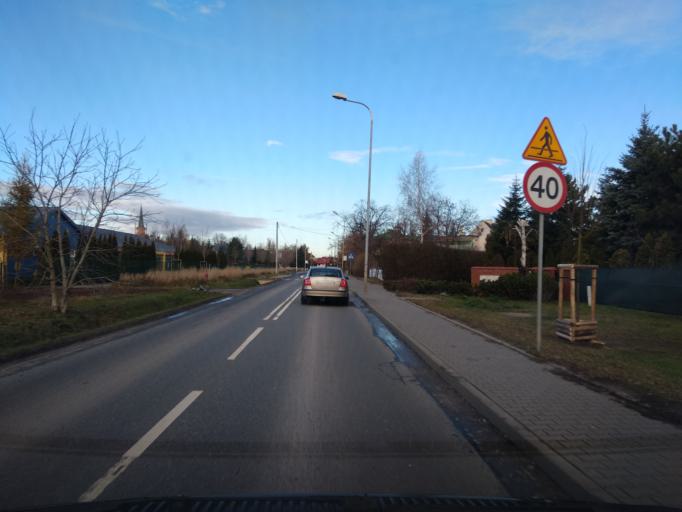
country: PL
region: Lower Silesian Voivodeship
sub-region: Powiat wroclawski
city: Zerniki Wroclawskie
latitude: 51.0539
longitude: 17.0274
